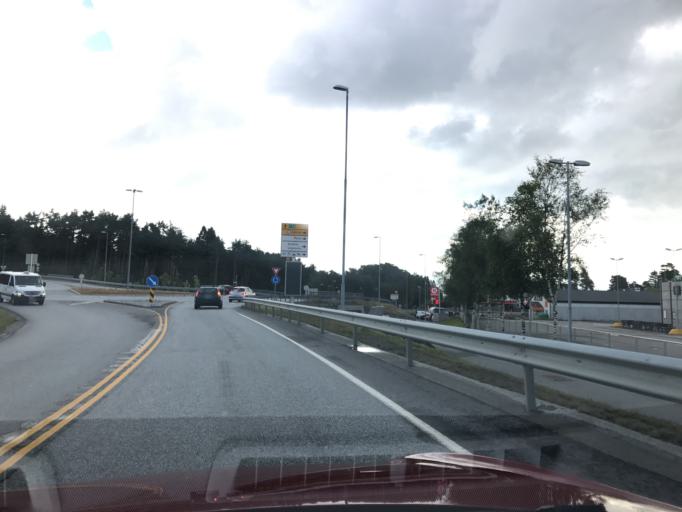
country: NO
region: Hordaland
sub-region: Stord
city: Leirvik
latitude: 59.7744
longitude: 5.4838
